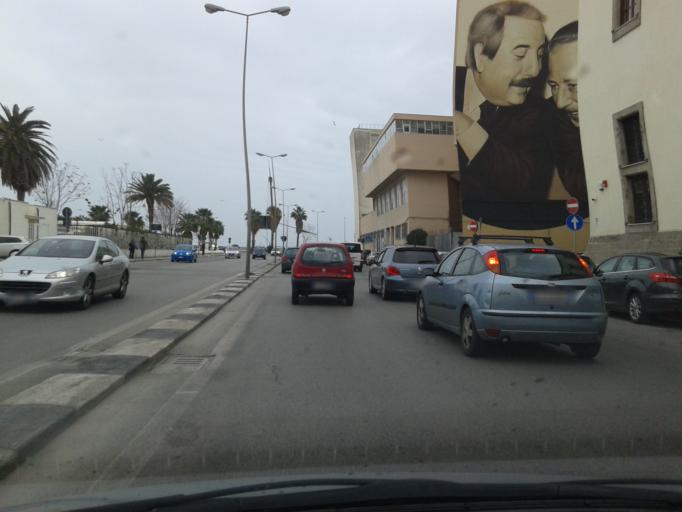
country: IT
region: Sicily
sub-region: Palermo
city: Palermo
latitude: 38.1196
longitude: 13.3695
